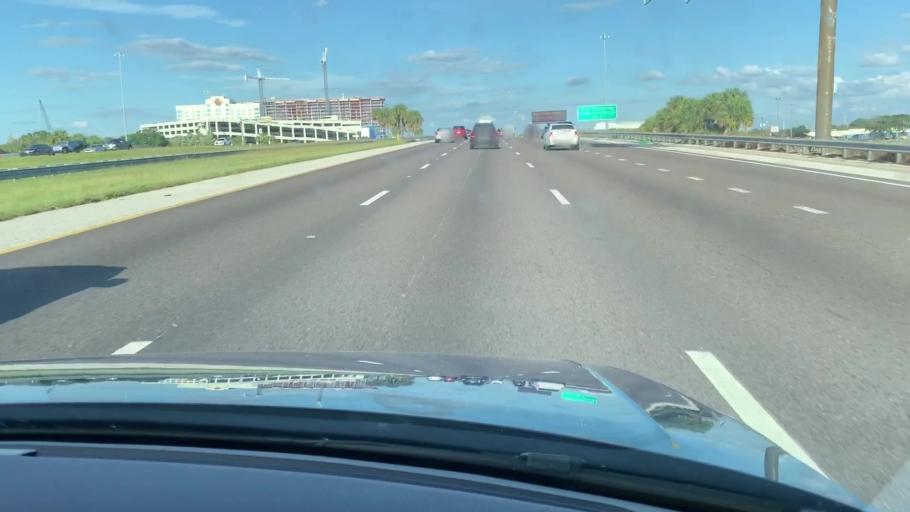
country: US
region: Florida
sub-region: Hillsborough County
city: East Lake-Orient Park
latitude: 27.9881
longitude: -82.3747
